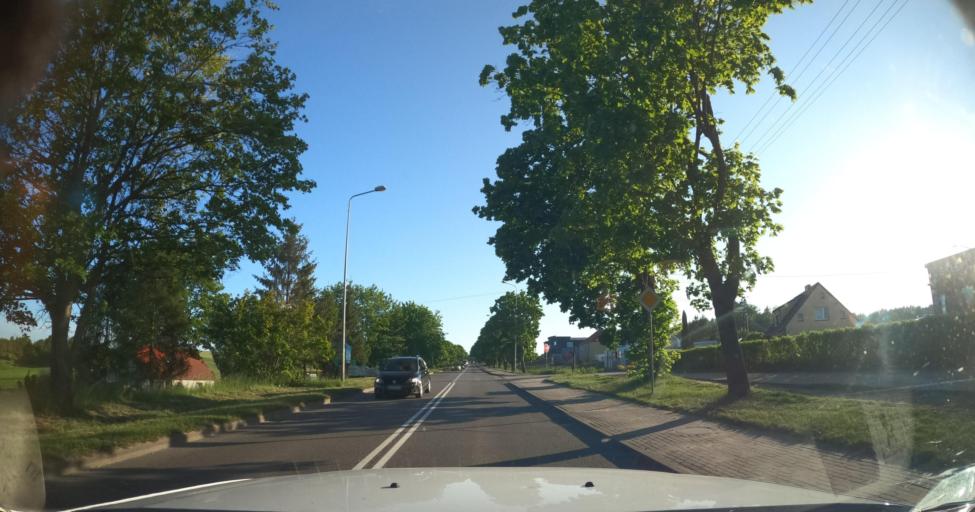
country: PL
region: Pomeranian Voivodeship
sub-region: Powiat kartuski
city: Zukowo
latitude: 54.3321
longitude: 18.3312
